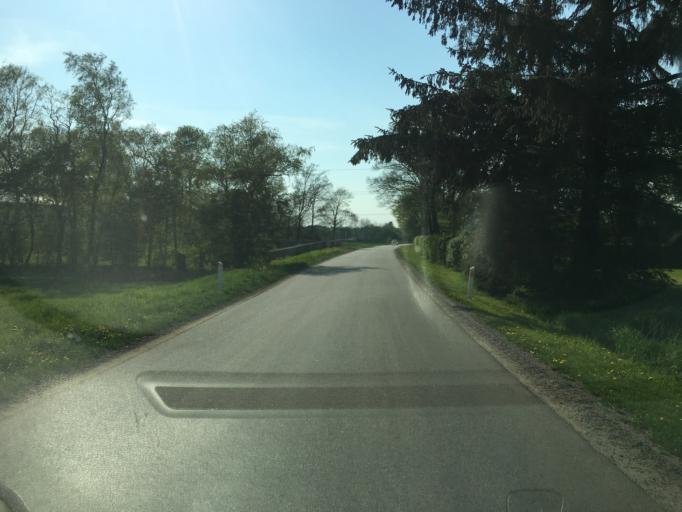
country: DK
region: South Denmark
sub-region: Haderslev Kommune
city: Vojens
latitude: 55.2319
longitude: 9.3424
